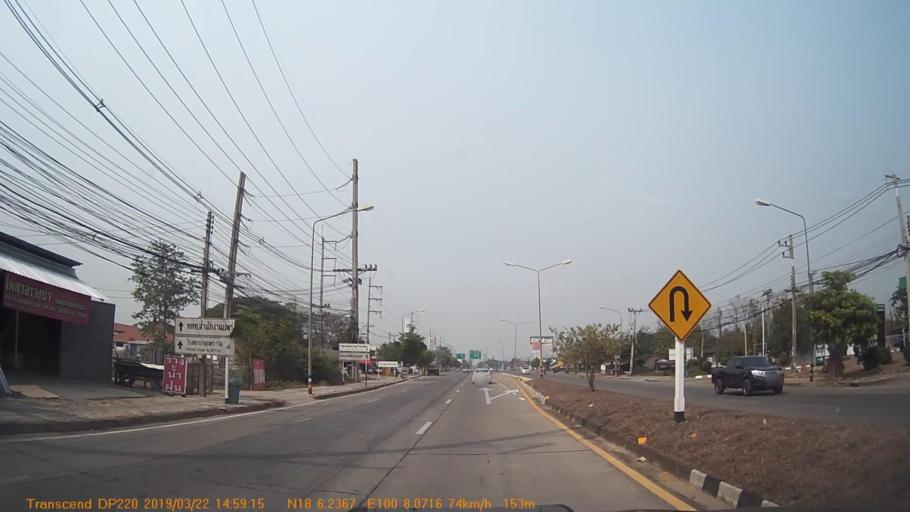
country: TH
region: Phrae
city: Phrae
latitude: 18.1043
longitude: 100.1347
